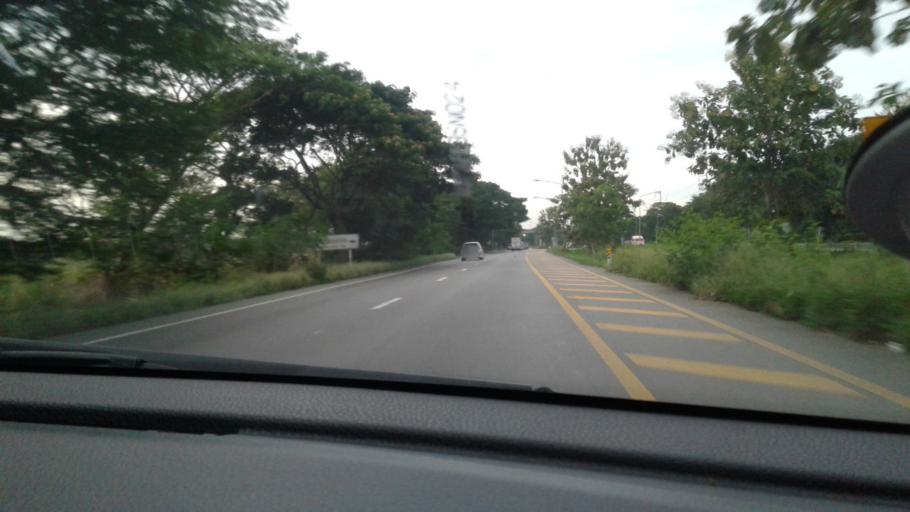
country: TH
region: Prachuap Khiri Khan
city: Hua Hin
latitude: 12.5279
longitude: 99.8791
